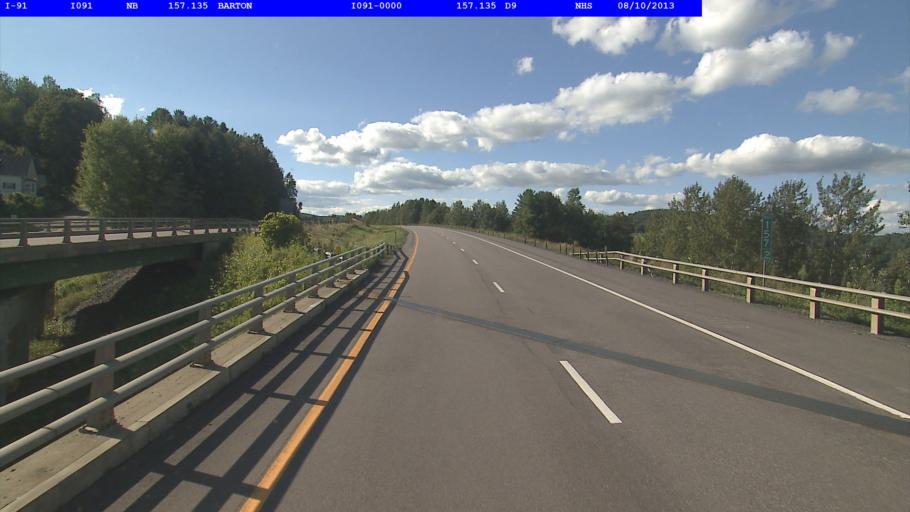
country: US
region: Vermont
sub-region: Orleans County
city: Newport
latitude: 44.7508
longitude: -72.1919
